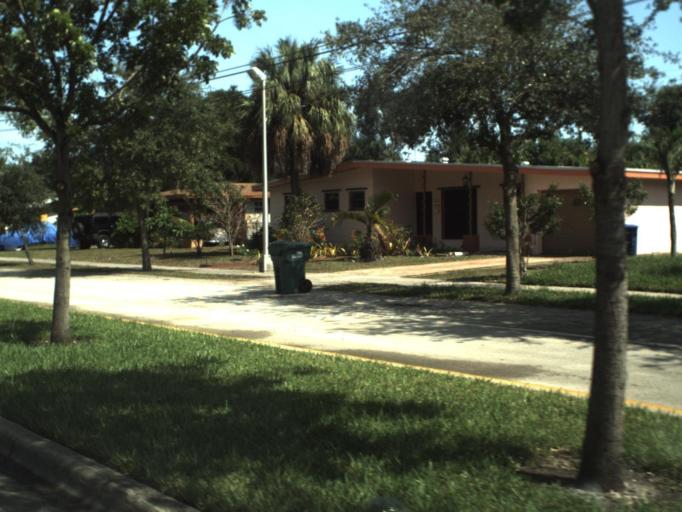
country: US
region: Florida
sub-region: Miami-Dade County
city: Carol City
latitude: 25.9410
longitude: -80.2409
